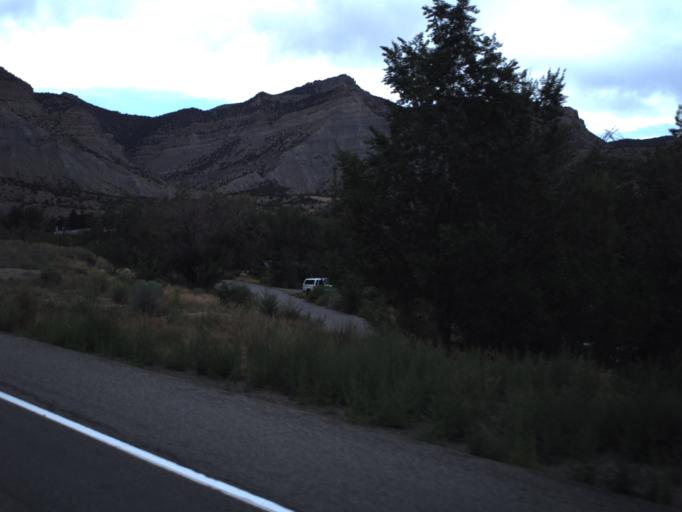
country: US
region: Utah
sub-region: Carbon County
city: Helper
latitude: 39.6834
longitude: -110.8579
